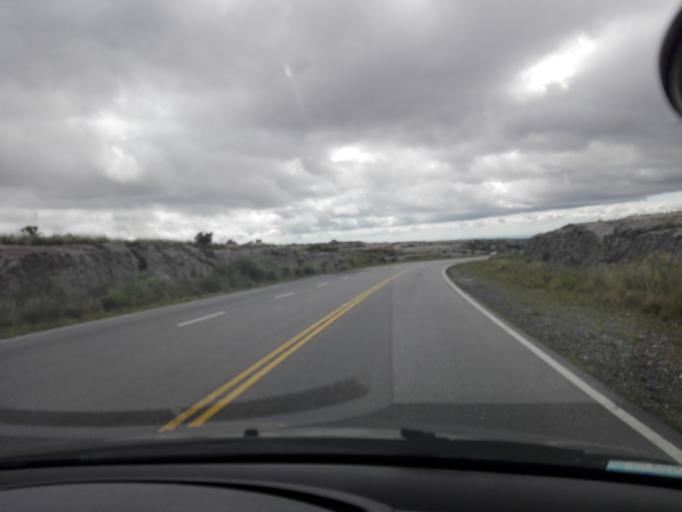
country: AR
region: Cordoba
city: Mina Clavero
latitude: -31.6170
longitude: -64.8774
